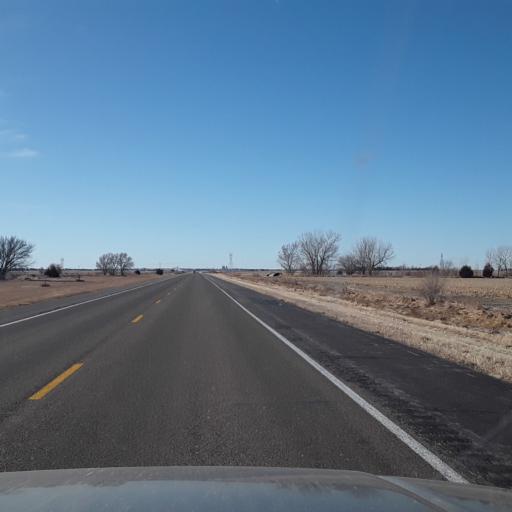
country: US
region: Nebraska
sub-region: Kearney County
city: Minden
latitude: 40.5358
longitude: -98.8672
